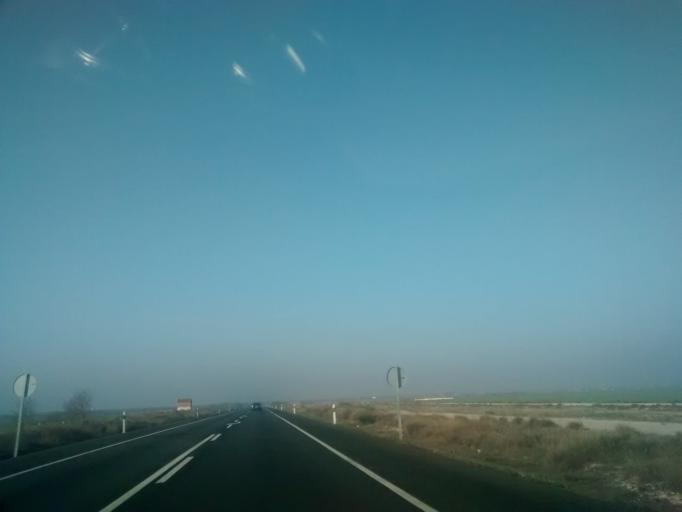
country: ES
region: Aragon
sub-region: Provincia de Huesca
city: Candasnos
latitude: 41.5185
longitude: 0.1380
